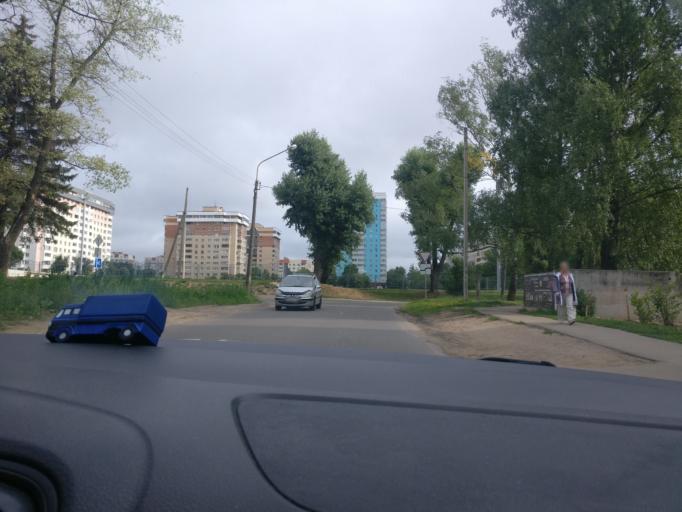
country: BY
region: Minsk
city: Minsk
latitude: 53.8741
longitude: 27.5552
